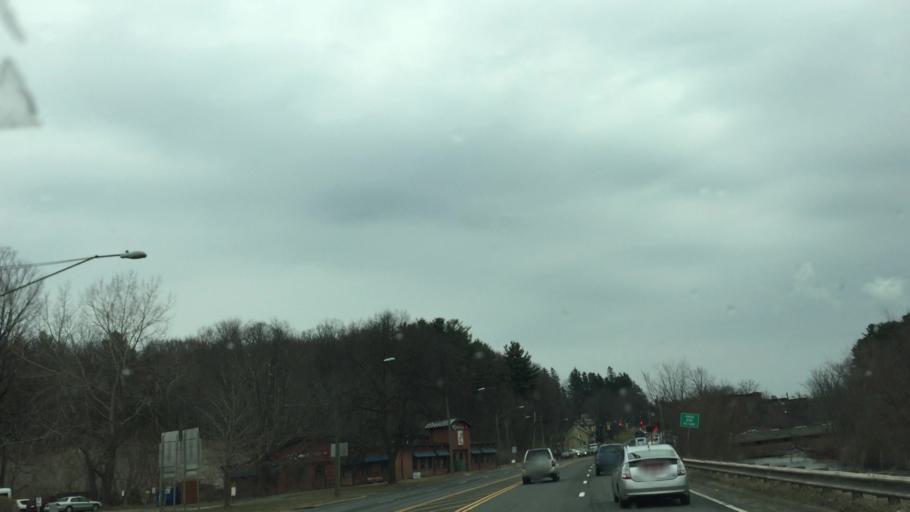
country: US
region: Massachusetts
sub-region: Berkshire County
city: Dalton
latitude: 42.4693
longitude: -73.1991
